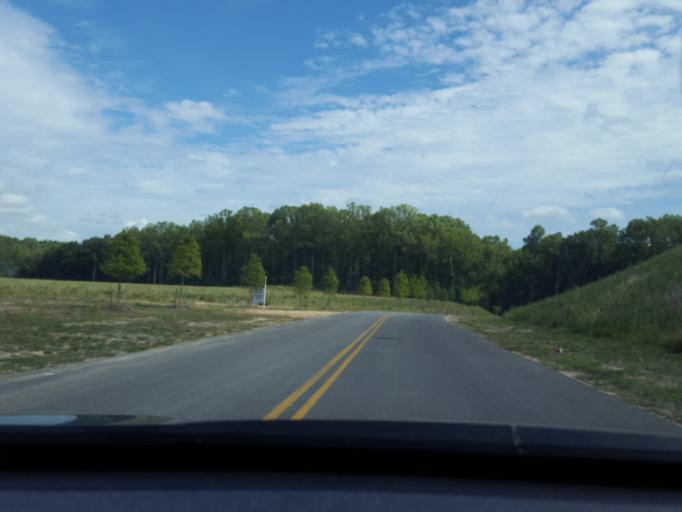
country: US
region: Maryland
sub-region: Prince George's County
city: Mellwood
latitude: 38.8158
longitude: -76.8274
